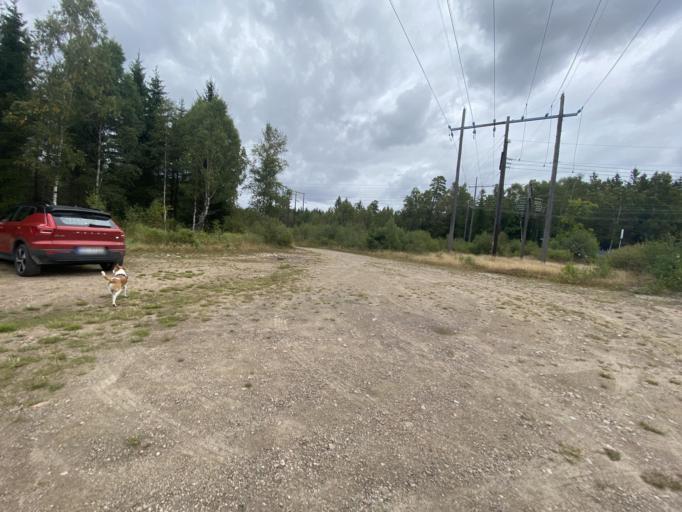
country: SE
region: Kronoberg
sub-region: Markaryds Kommun
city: Markaryd
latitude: 56.4868
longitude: 13.5978
